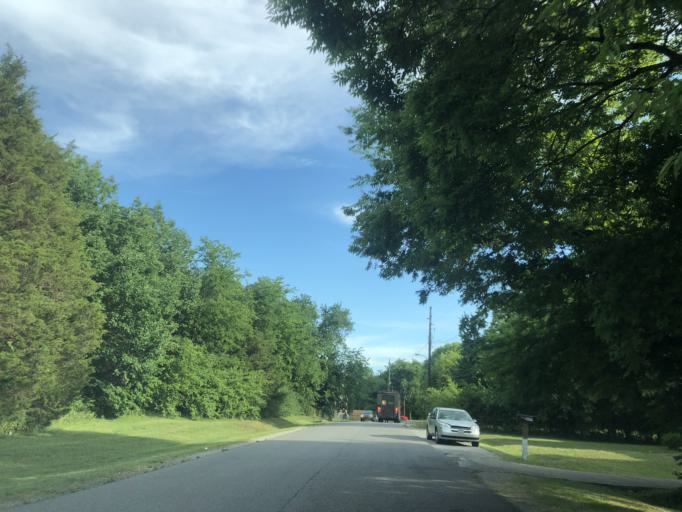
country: US
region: Tennessee
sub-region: Davidson County
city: Nashville
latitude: 36.2134
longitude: -86.8446
